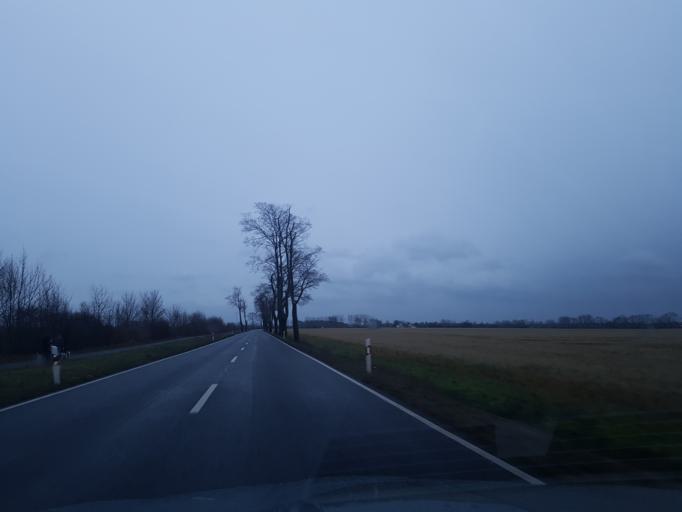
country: DE
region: Brandenburg
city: Elsterwerda
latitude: 51.4414
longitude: 13.5149
